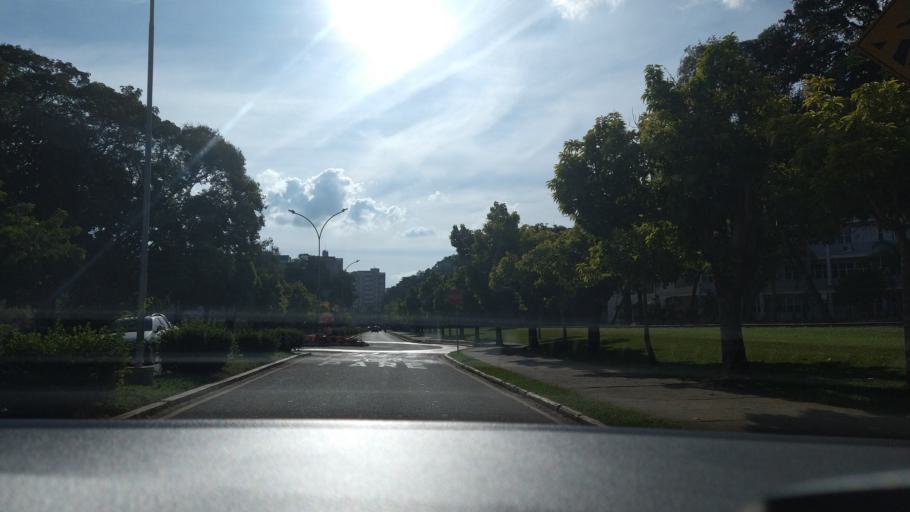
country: BR
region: Minas Gerais
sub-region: Vicosa
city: Vicosa
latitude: -20.7585
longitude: -42.8724
